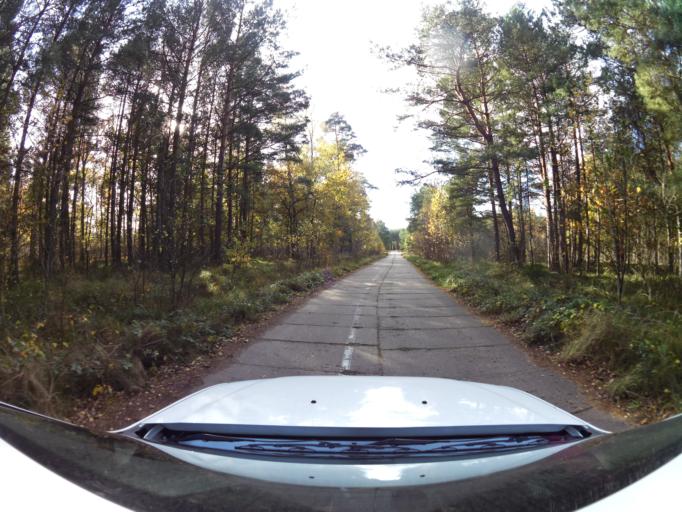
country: PL
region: West Pomeranian Voivodeship
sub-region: Powiat gryficki
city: Cerkwica
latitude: 54.1005
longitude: 15.1415
